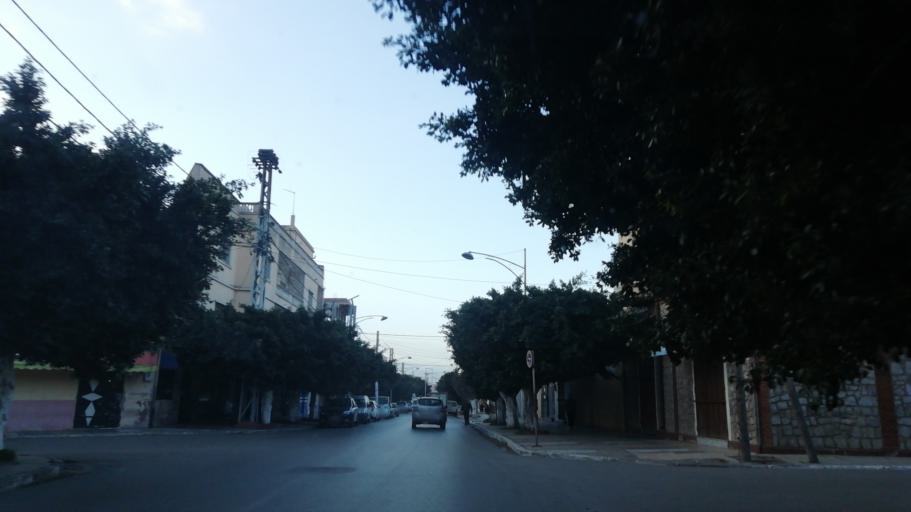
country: DZ
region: Oran
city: Oran
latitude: 35.6801
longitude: -0.6562
